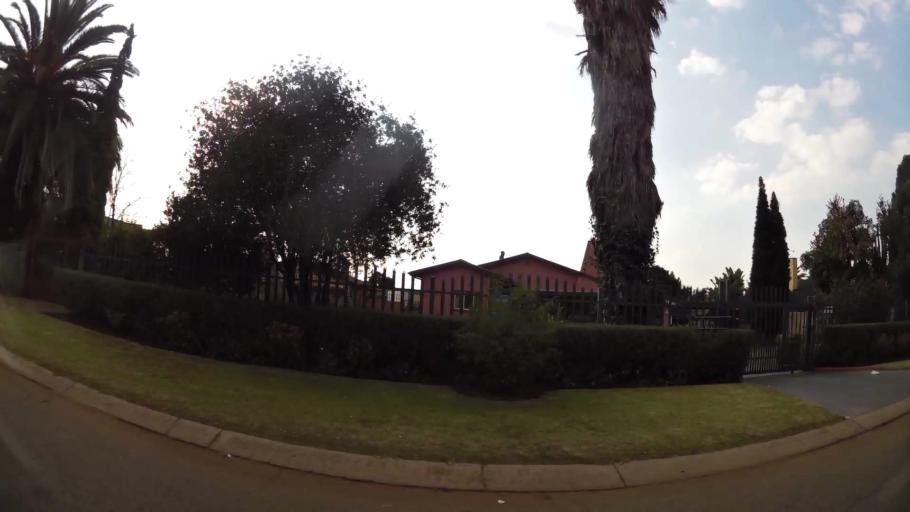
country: ZA
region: Gauteng
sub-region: City of Johannesburg Metropolitan Municipality
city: Modderfontein
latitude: -26.1117
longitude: 28.2038
